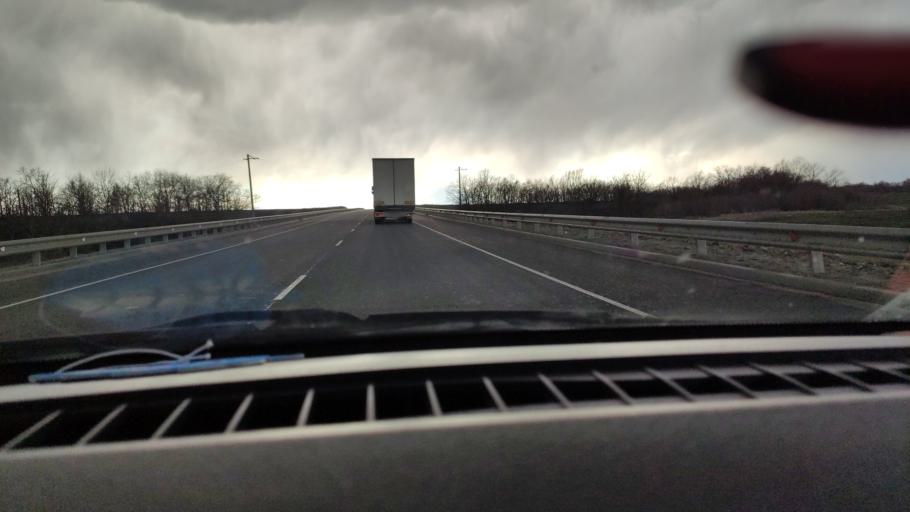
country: RU
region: Saratov
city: Yelshanka
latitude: 51.8309
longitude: 46.4432
